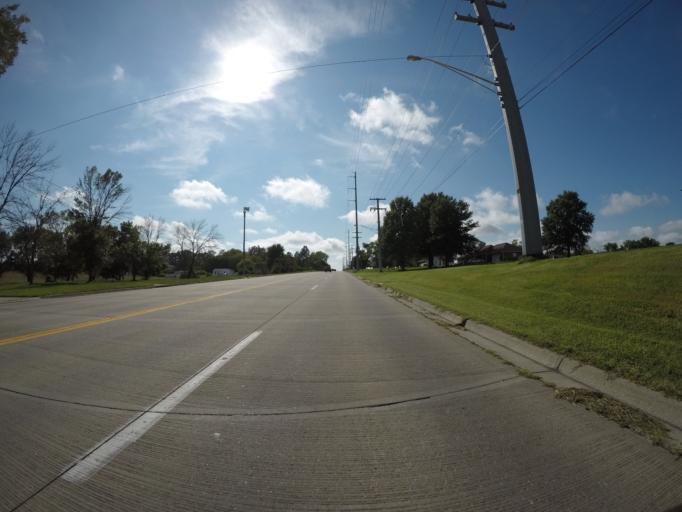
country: US
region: Kansas
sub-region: Wyandotte County
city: Bonner Springs
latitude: 39.1287
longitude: -94.8553
